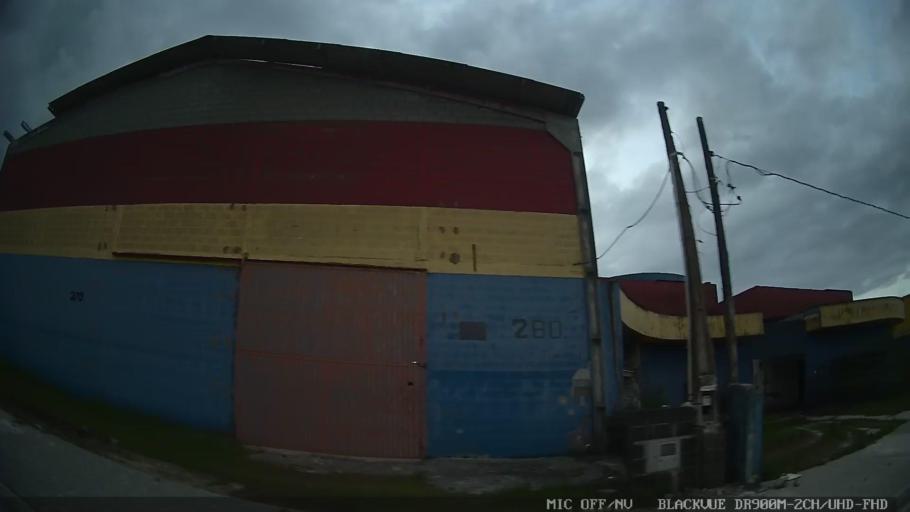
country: BR
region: Sao Paulo
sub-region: Itanhaem
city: Itanhaem
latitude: -24.1908
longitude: -46.8322
